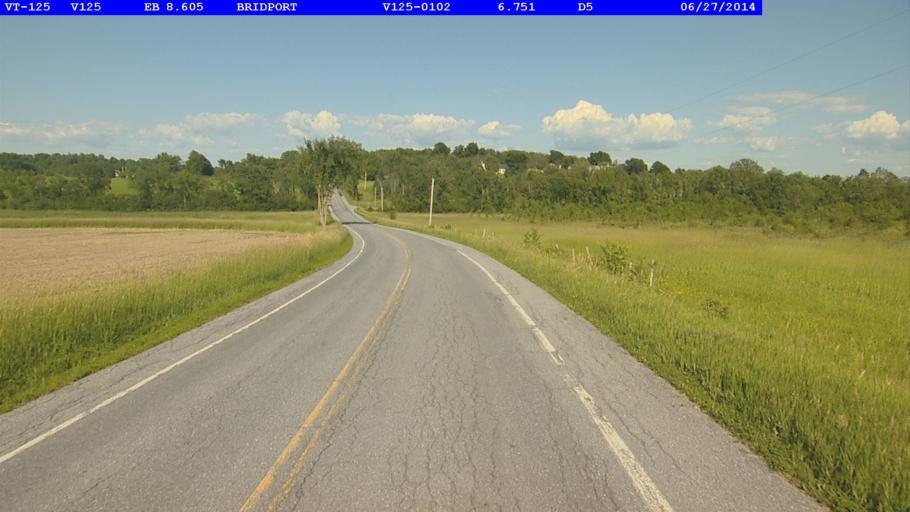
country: US
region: Vermont
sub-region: Addison County
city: Middlebury (village)
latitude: 43.9894
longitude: -73.2829
